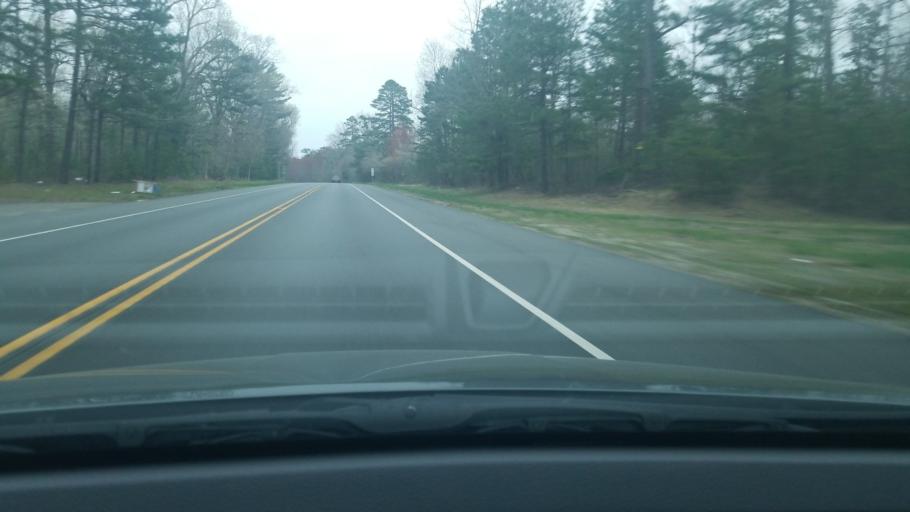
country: US
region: New Jersey
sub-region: Burlington County
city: Presidential Lakes Estates
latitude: 39.8918
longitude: -74.6226
